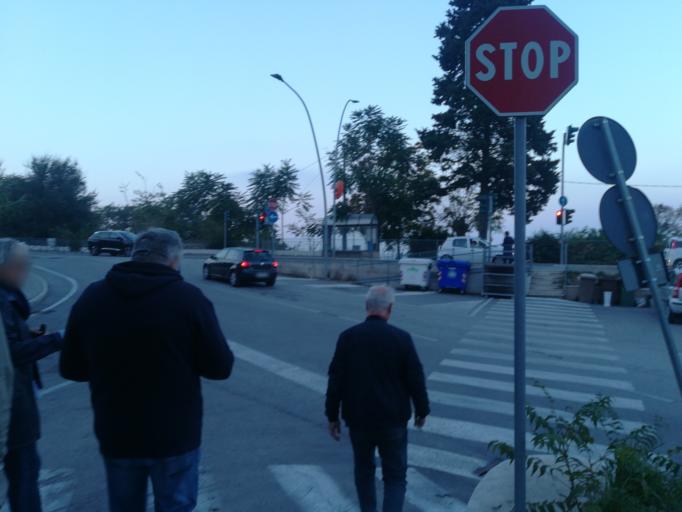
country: IT
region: The Marches
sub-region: Provincia di Macerata
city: Macerata
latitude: 43.2945
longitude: 13.4640
